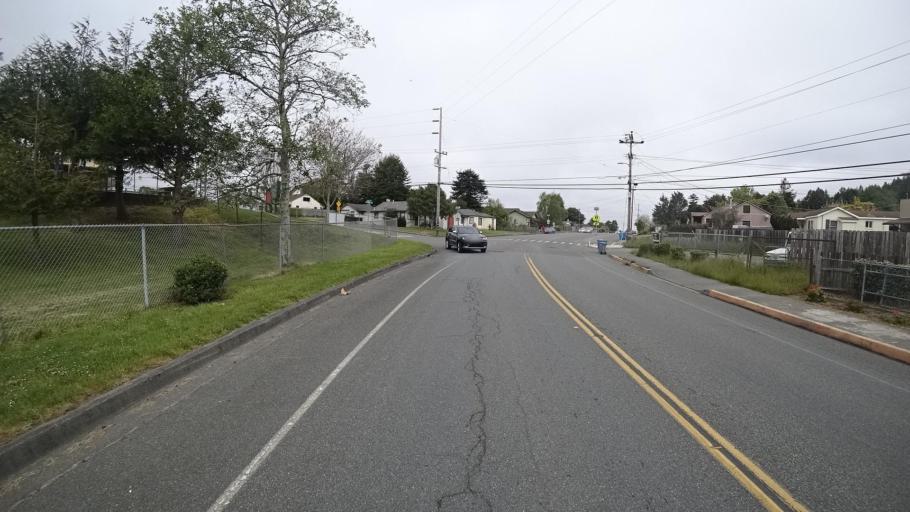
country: US
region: California
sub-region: Humboldt County
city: Cutten
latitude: 40.7709
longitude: -124.1614
